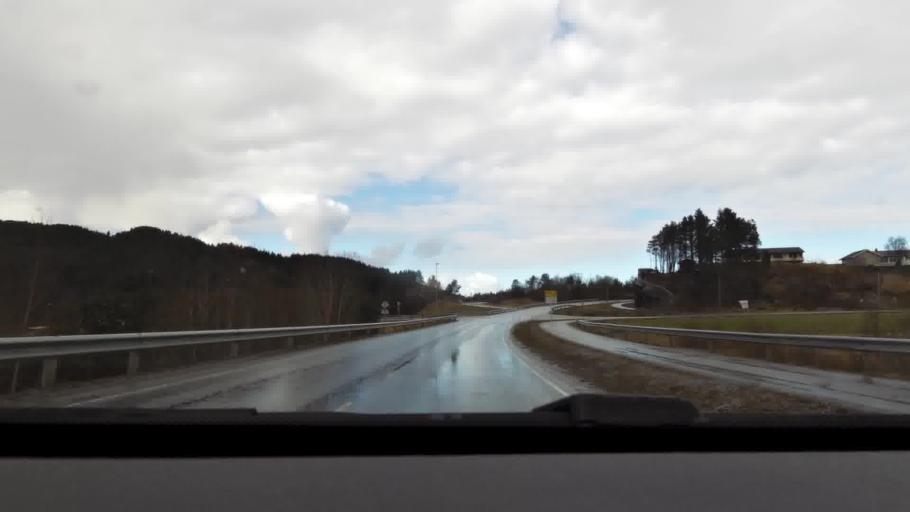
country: NO
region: More og Romsdal
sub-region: Kristiansund
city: Rensvik
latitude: 63.1053
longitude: 7.8216
